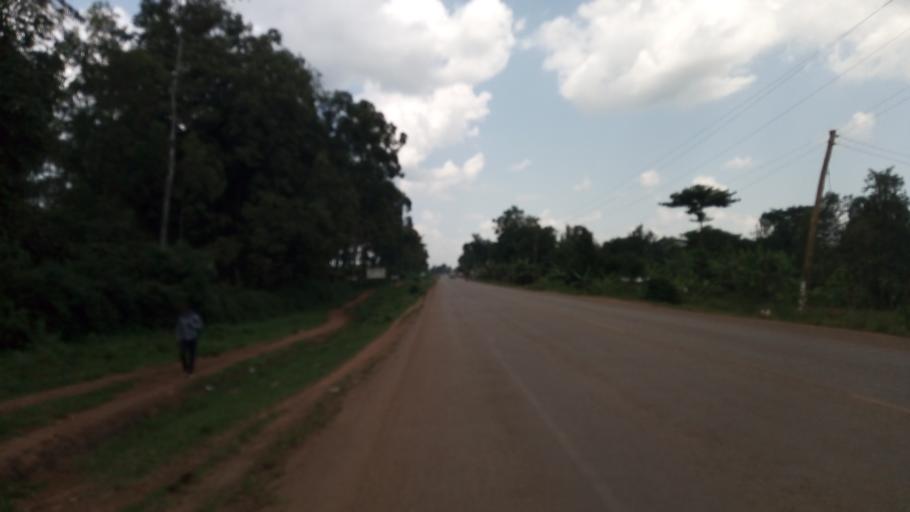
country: UG
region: Eastern Region
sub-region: Mbale District
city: Mbale
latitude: 1.0358
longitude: 34.1774
